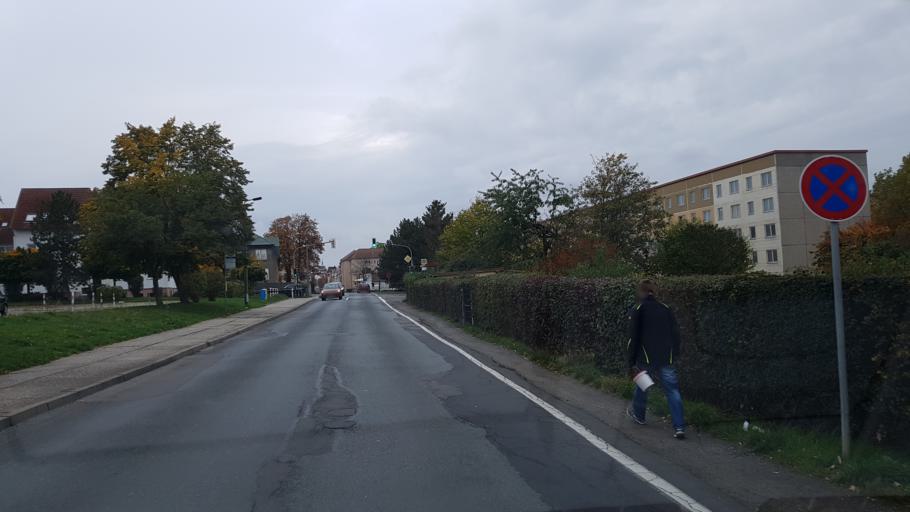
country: DE
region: Saxony
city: Wurzen
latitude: 51.3781
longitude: 12.7376
